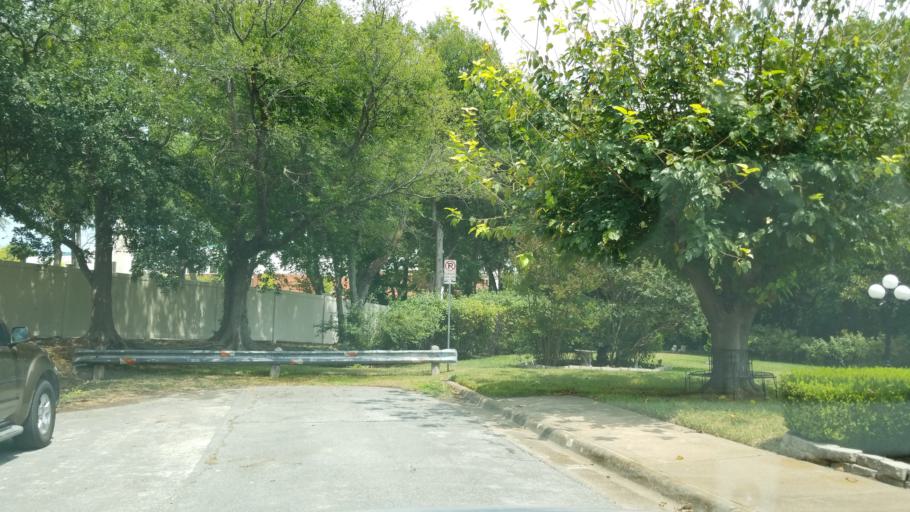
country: US
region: Texas
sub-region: Dallas County
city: Duncanville
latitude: 32.6601
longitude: -96.8494
